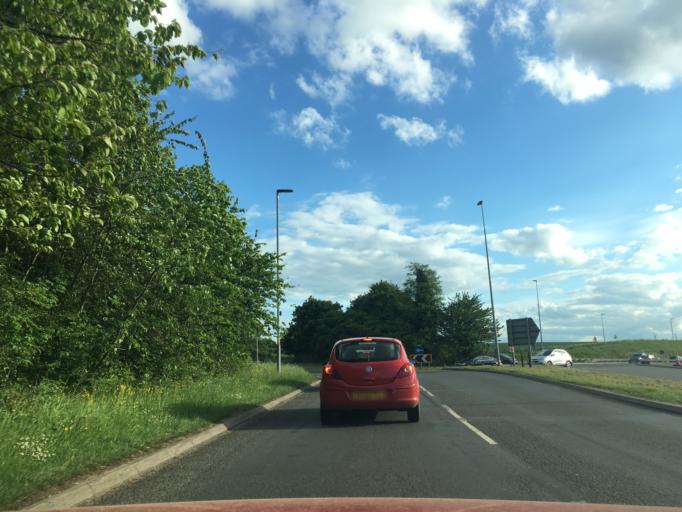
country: GB
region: England
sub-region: Worcestershire
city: Worcester
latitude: 52.1729
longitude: -2.1842
